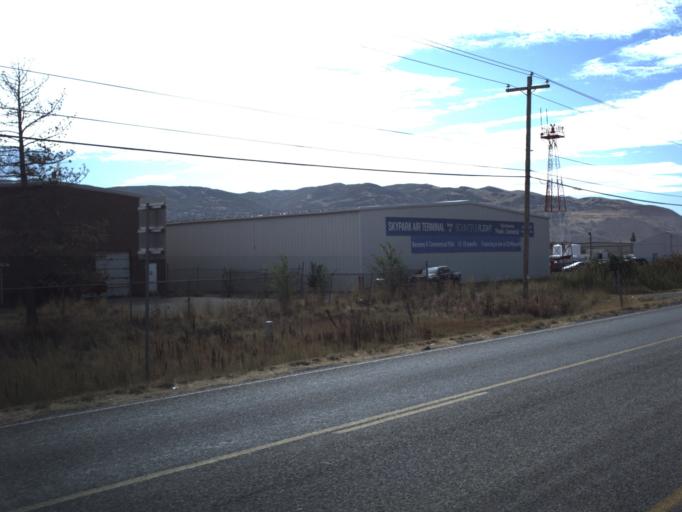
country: US
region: Utah
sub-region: Davis County
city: North Salt Lake
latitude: 40.8687
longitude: -111.9300
